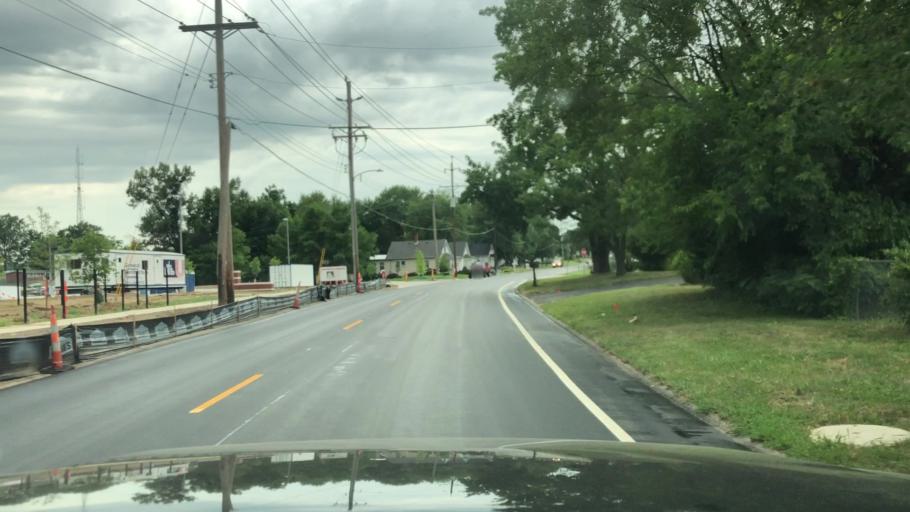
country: US
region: Missouri
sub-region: Saint Charles County
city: Saint Charles
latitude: 38.7733
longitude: -90.5024
